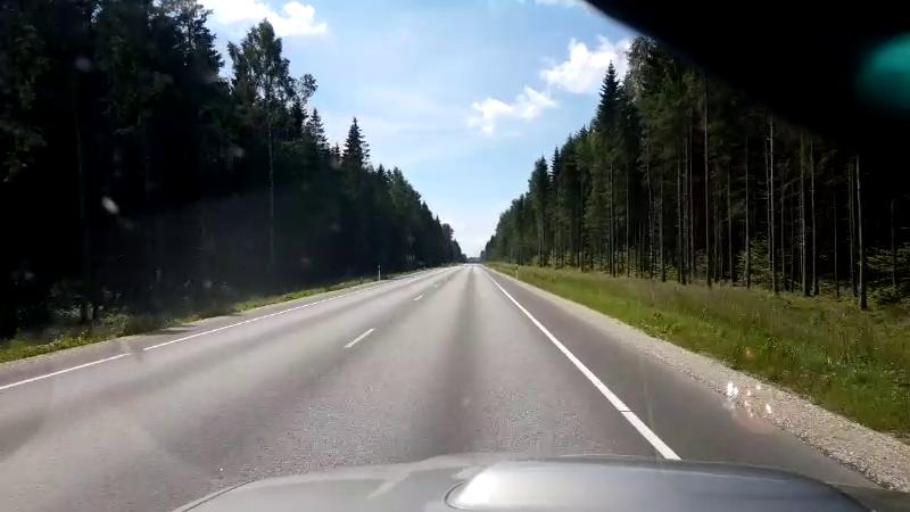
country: EE
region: Jaervamaa
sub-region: Paide linn
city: Paide
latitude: 58.9579
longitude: 25.6544
